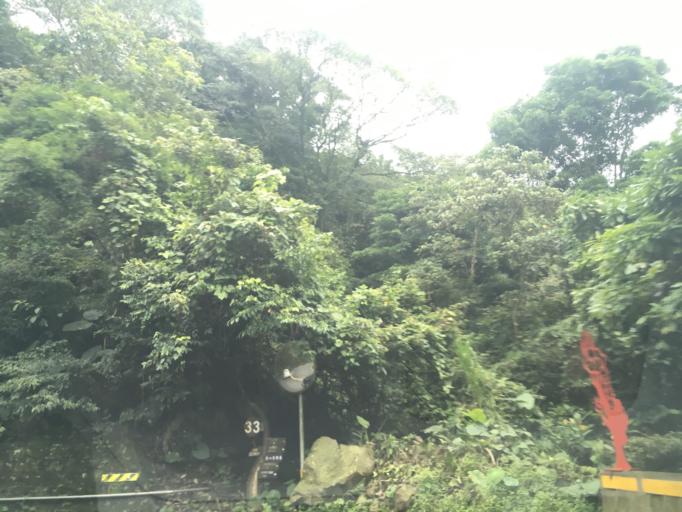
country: TW
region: Taiwan
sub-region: Yunlin
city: Douliu
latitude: 23.5618
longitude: 120.5966
